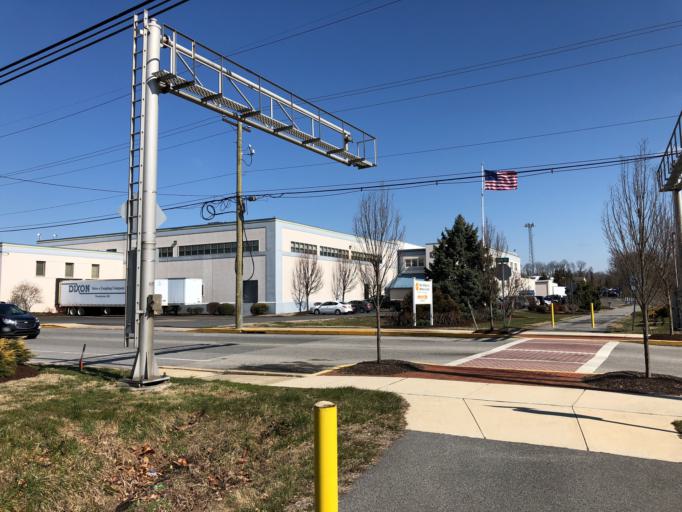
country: US
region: Maryland
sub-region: Kent County
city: Chestertown
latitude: 39.2139
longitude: -76.0740
